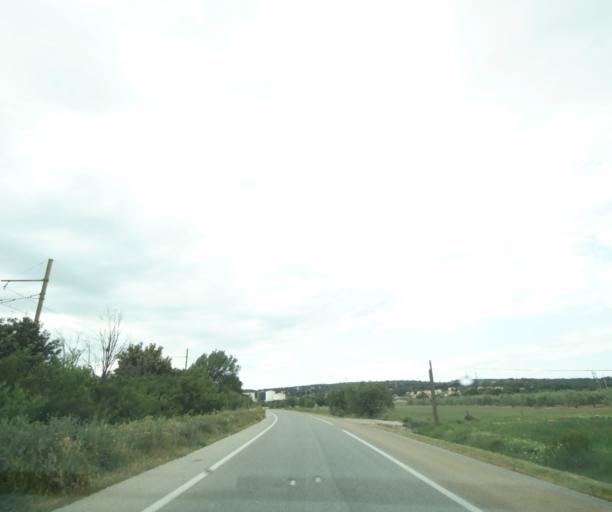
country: FR
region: Provence-Alpes-Cote d'Azur
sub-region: Departement des Bouches-du-Rhone
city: Rognac
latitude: 43.5010
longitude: 5.2263
